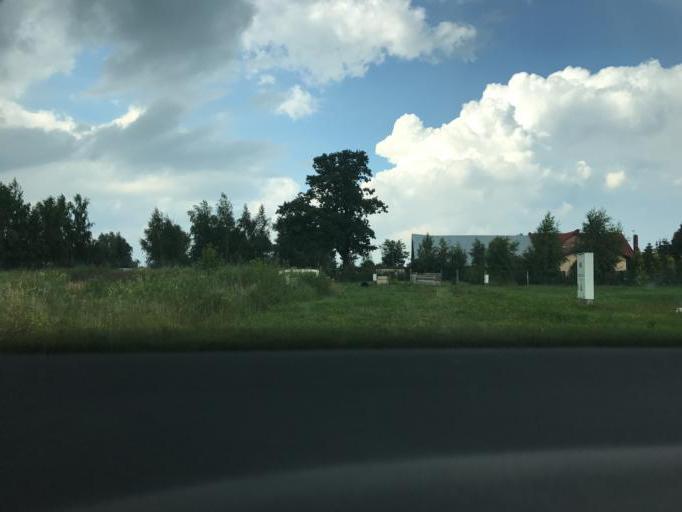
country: PL
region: Pomeranian Voivodeship
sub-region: Powiat gdanski
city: Cedry Wielkie
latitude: 54.3379
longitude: 18.8161
